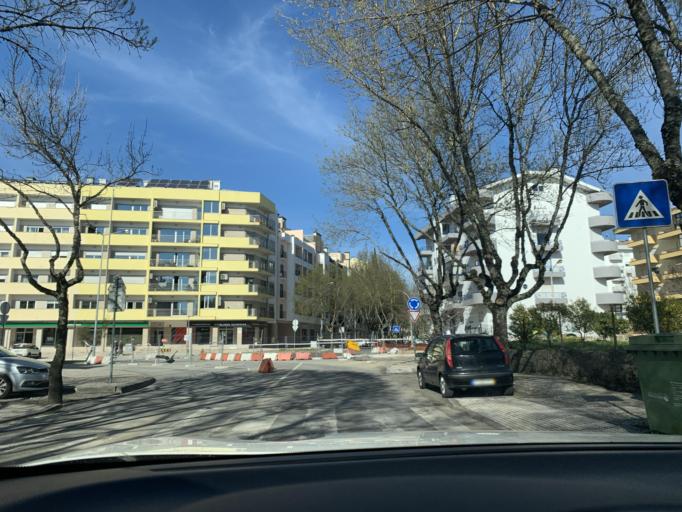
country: PT
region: Viseu
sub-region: Viseu
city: Viseu
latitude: 40.6468
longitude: -7.9143
